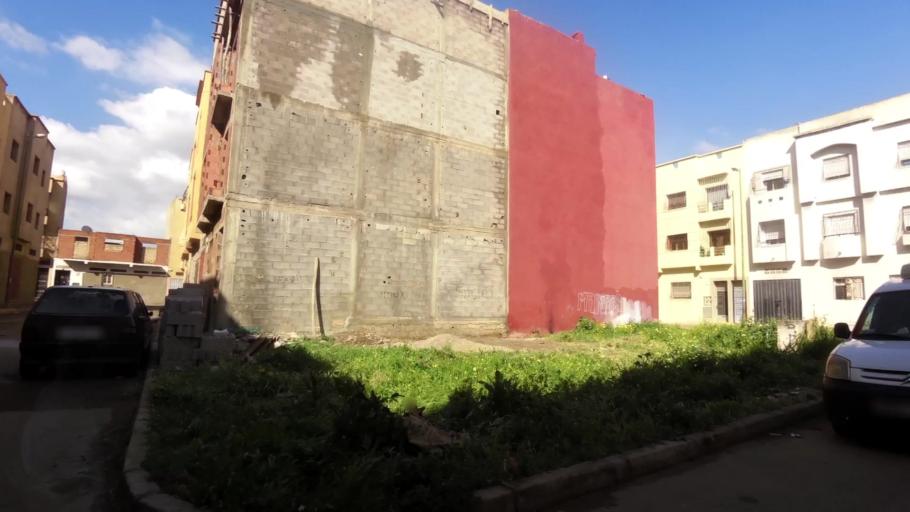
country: MA
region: Chaouia-Ouardigha
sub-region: Settat Province
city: Berrechid
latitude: 33.2558
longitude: -7.5718
